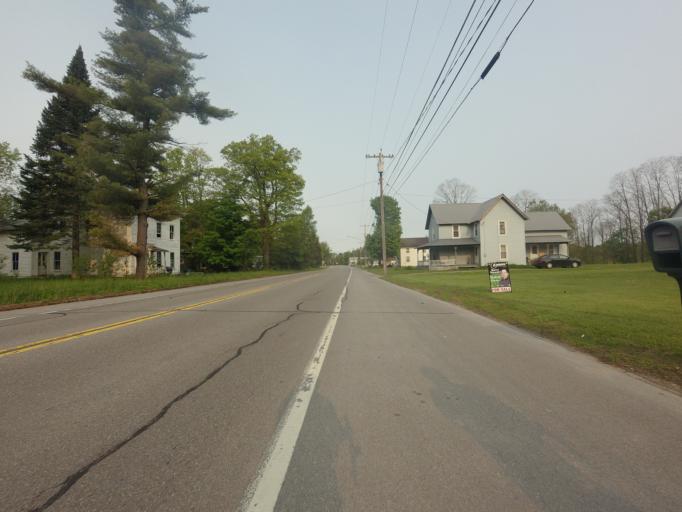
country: US
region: New York
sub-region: Jefferson County
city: Carthage
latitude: 44.0692
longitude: -75.4975
